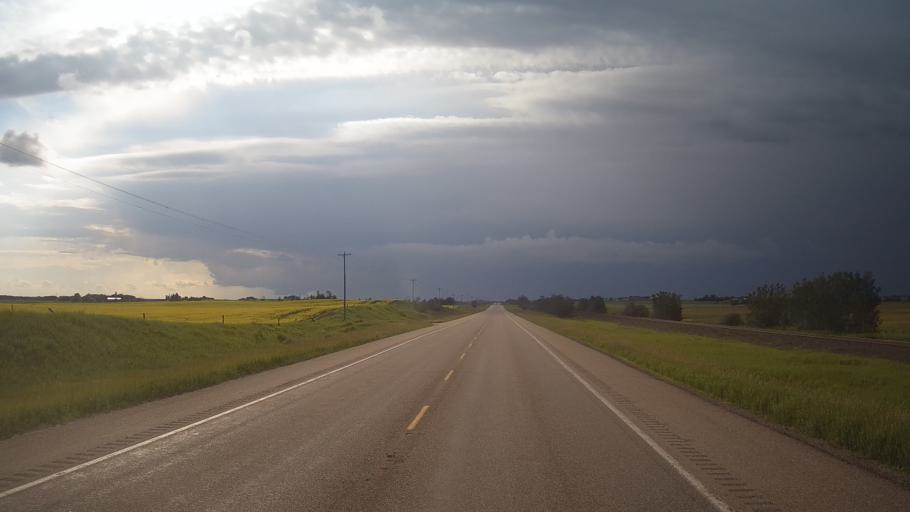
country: CA
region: Alberta
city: Vegreville
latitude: 53.2122
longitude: -112.1762
